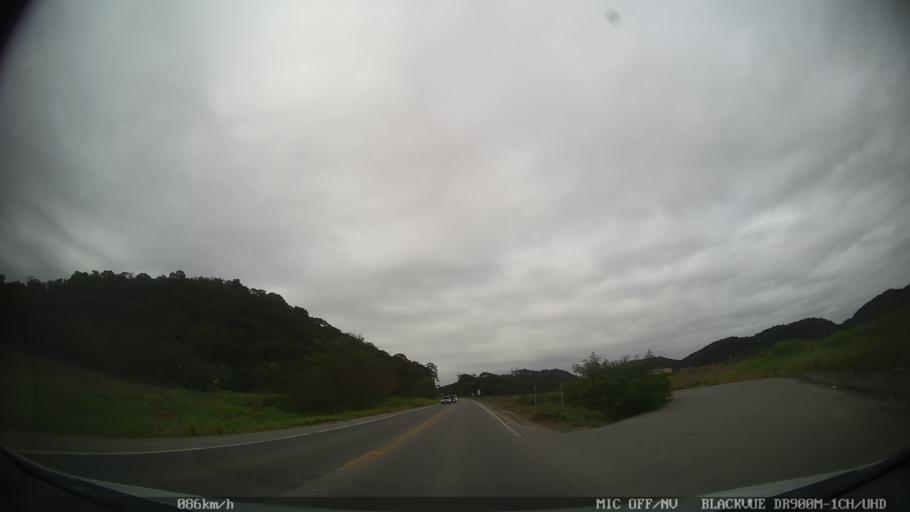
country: BR
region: Santa Catarina
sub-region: Joinville
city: Joinville
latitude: -26.2611
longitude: -48.9130
